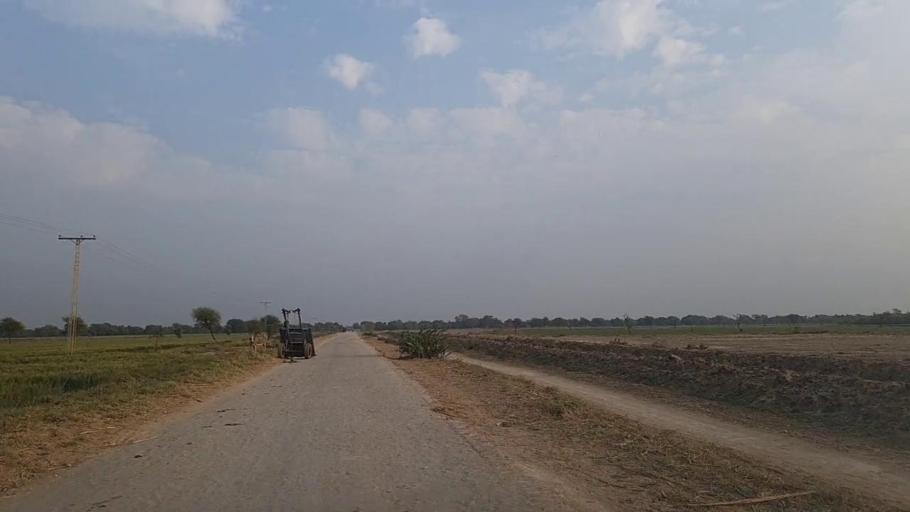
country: PK
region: Sindh
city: Mirwah Gorchani
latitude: 25.3036
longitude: 69.2166
